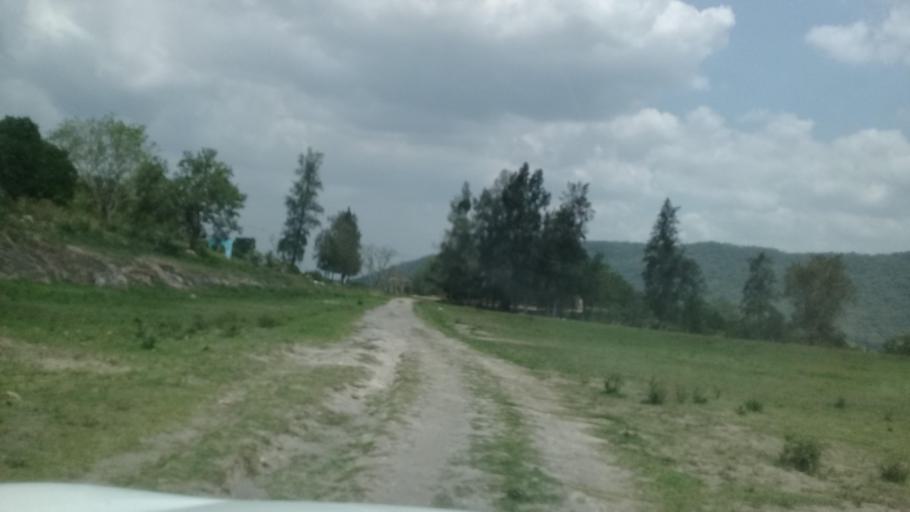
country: MX
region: Veracruz
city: Jalcomulco
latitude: 19.3843
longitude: -96.7937
